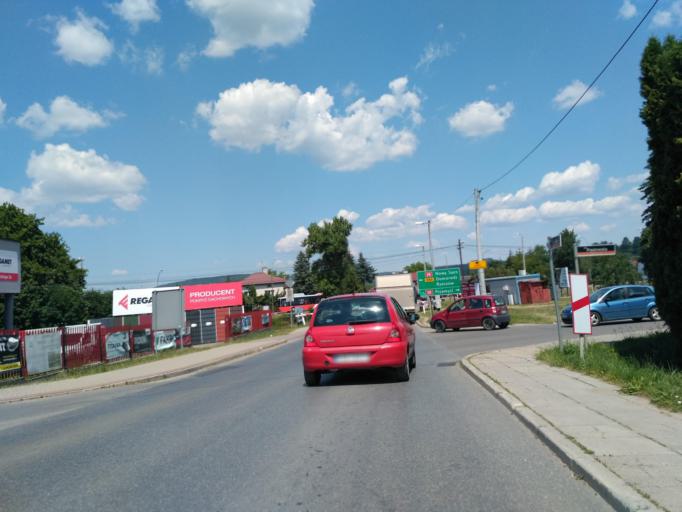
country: PL
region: Subcarpathian Voivodeship
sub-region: Powiat sanocki
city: Sanok
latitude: 49.5684
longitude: 22.1581
